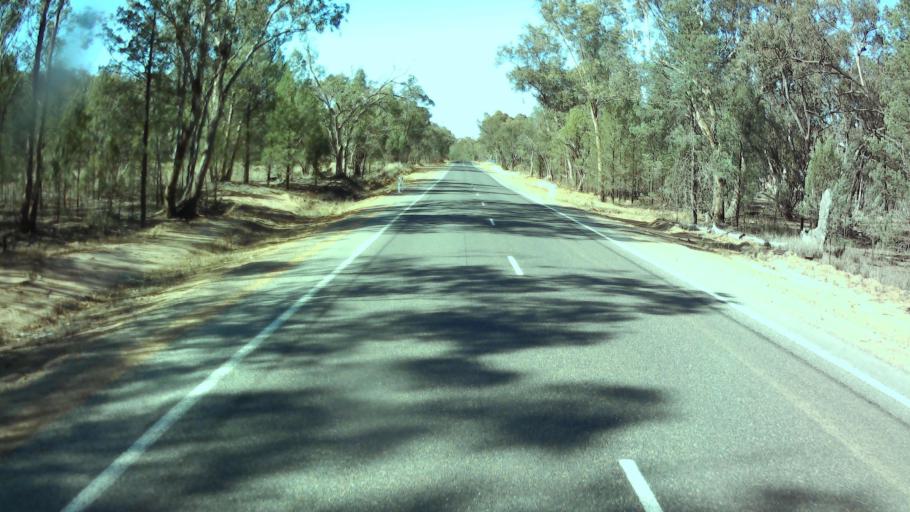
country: AU
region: New South Wales
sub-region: Weddin
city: Grenfell
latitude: -33.7493
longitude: 148.0859
